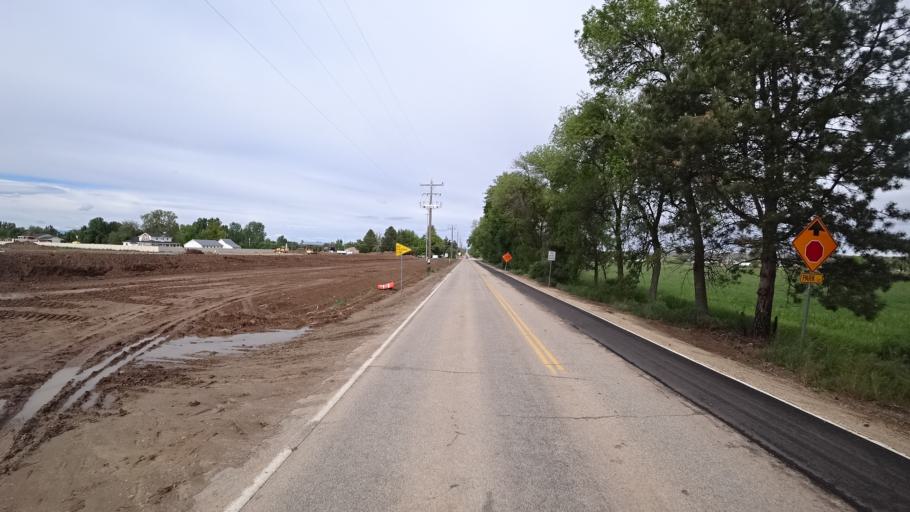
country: US
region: Idaho
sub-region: Ada County
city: Eagle
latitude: 43.7209
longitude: -116.4010
